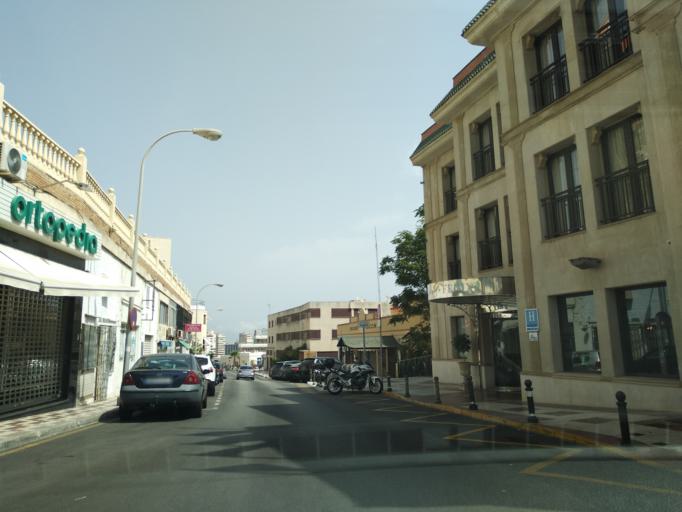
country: ES
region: Andalusia
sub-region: Provincia de Malaga
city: Torremolinos
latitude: 36.6237
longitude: -4.4966
